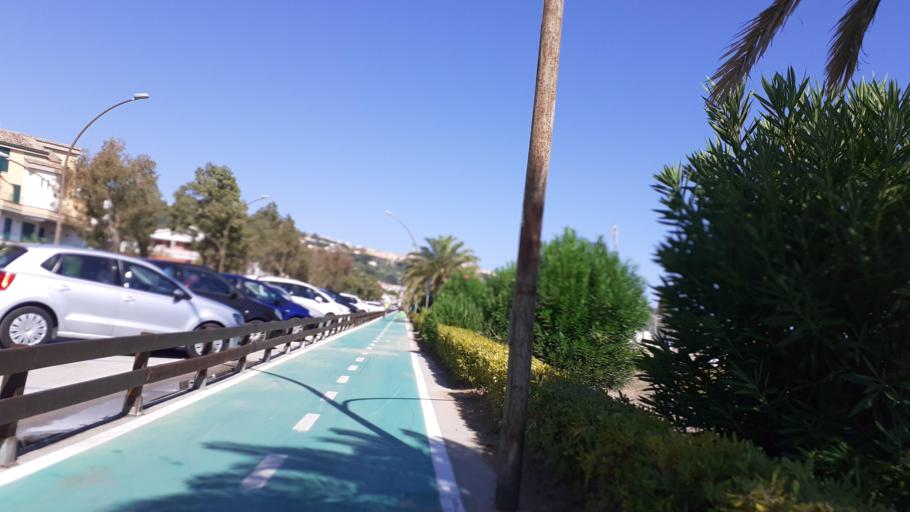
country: IT
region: Abruzzo
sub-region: Provincia di Chieti
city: Marina di Vasto
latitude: 42.0966
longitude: 14.7246
